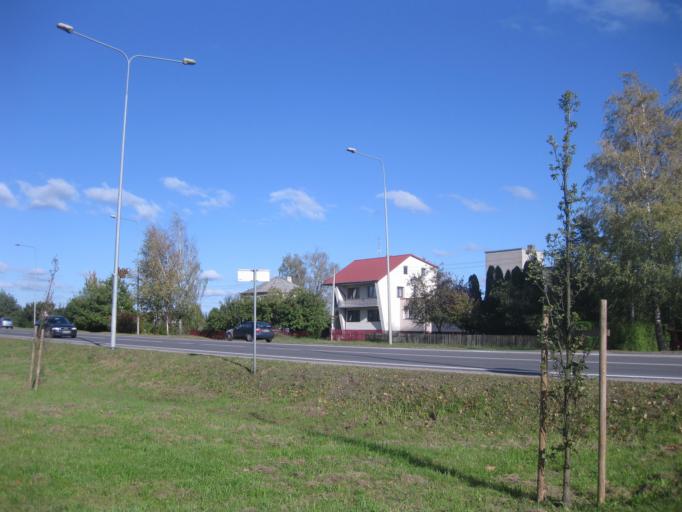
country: LT
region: Kauno apskritis
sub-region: Kauno rajonas
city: Garliava
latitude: 54.8405
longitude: 23.8777
